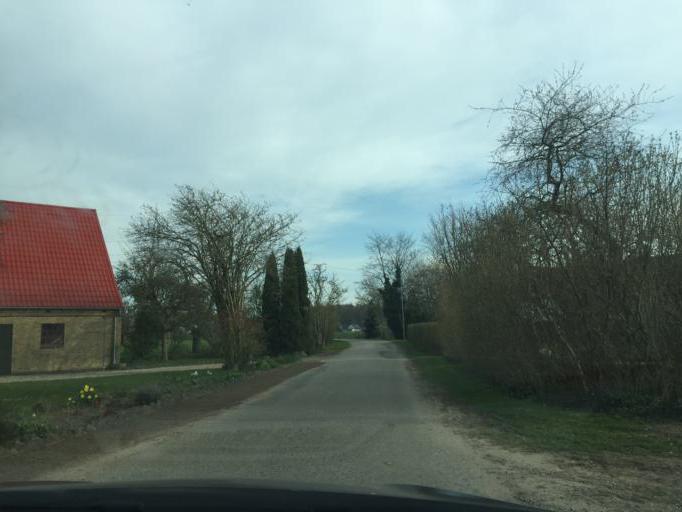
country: DK
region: South Denmark
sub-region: Faaborg-Midtfyn Kommune
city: Arslev
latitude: 55.3237
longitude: 10.5084
